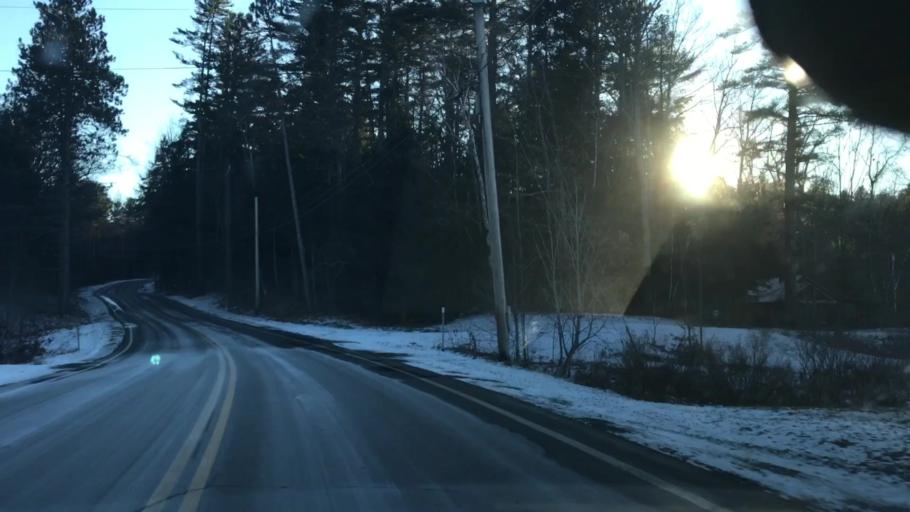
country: US
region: New Hampshire
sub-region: Grafton County
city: Lyme Town Offices
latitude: 43.8254
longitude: -72.1452
